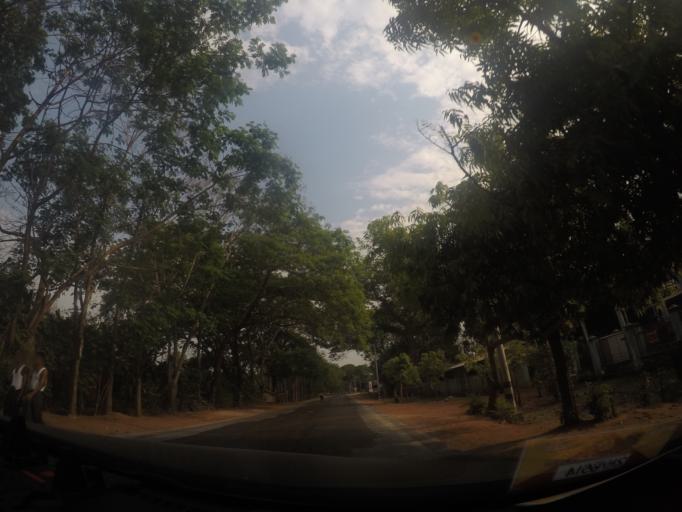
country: MM
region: Bago
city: Paungde
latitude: 18.2699
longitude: 95.6401
